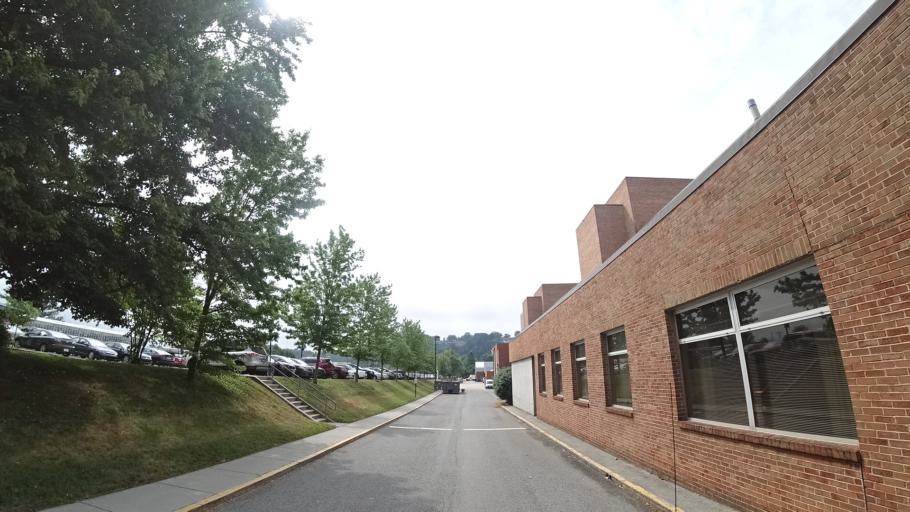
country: US
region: Tennessee
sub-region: Knox County
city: Knoxville
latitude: 35.9468
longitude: -83.9403
